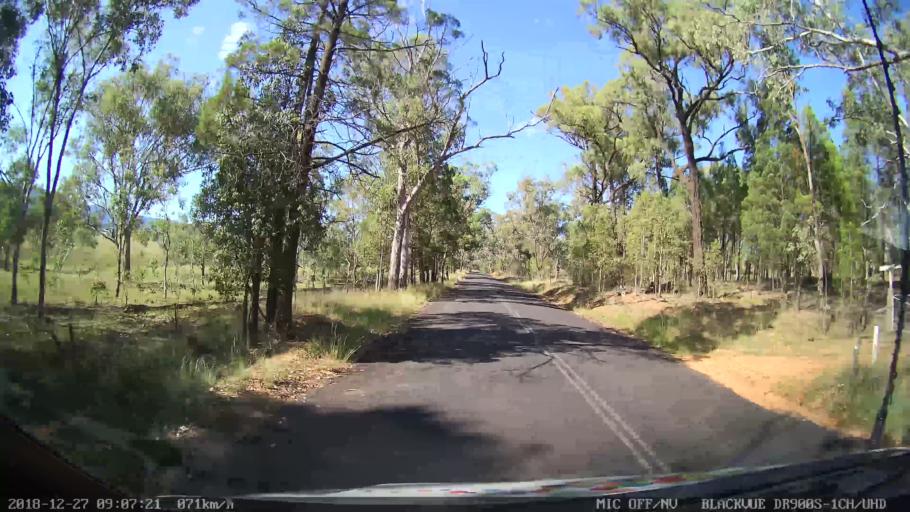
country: AU
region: New South Wales
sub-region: Lithgow
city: Portland
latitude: -33.1279
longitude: 150.1575
